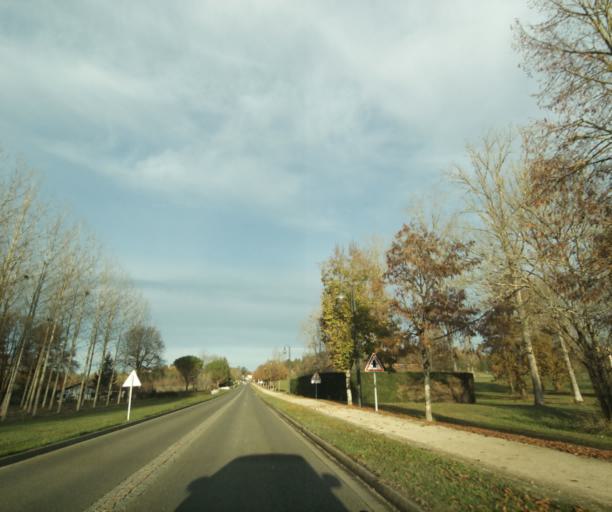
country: FR
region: Midi-Pyrenees
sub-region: Departement du Gers
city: Cazaubon
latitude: 43.9416
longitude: -0.0545
